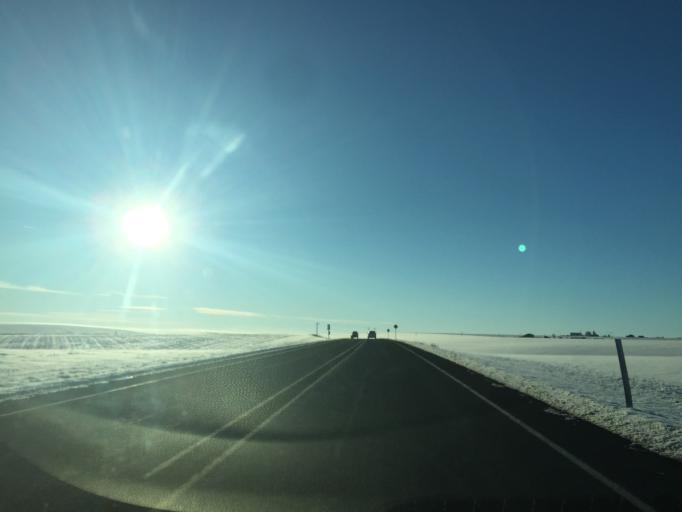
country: US
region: Washington
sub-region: Okanogan County
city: Coulee Dam
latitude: 47.7013
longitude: -118.9527
